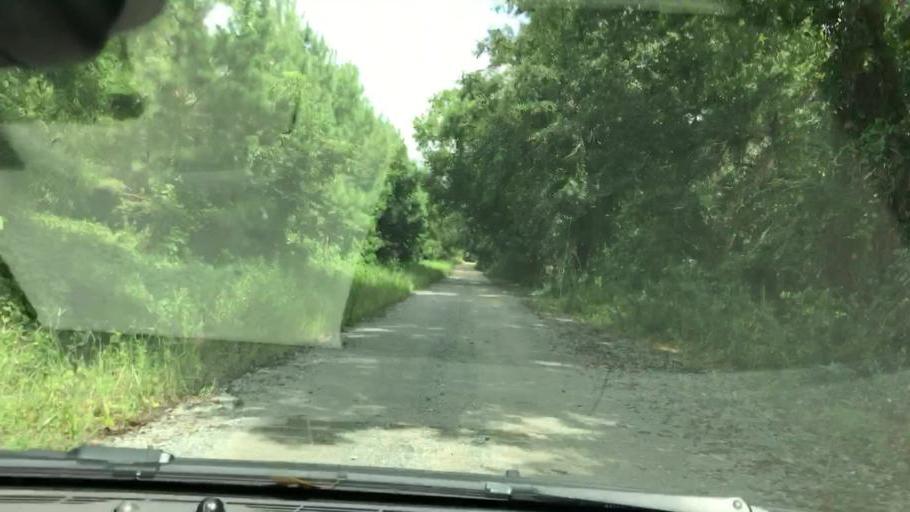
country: US
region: Georgia
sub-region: Clay County
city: Fort Gaines
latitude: 31.7220
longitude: -85.0729
